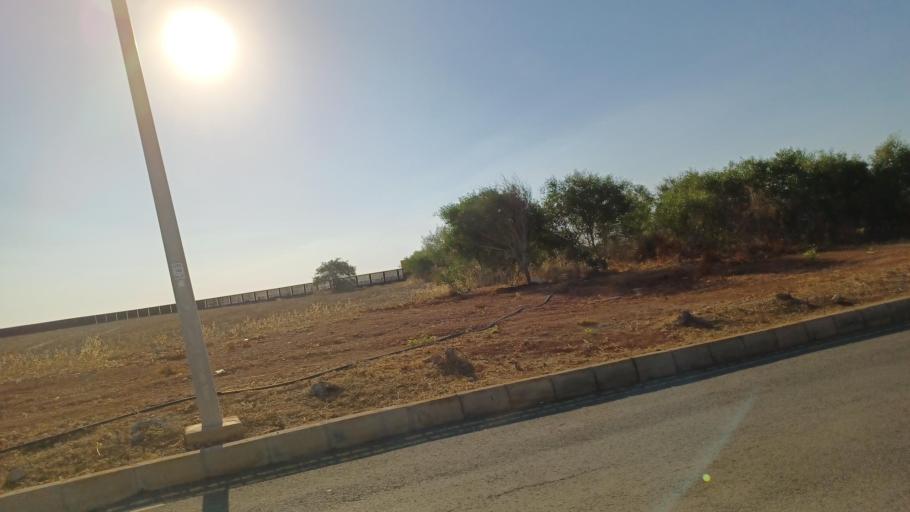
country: CY
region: Larnaka
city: Xylotymbou
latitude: 34.9964
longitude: 33.7424
